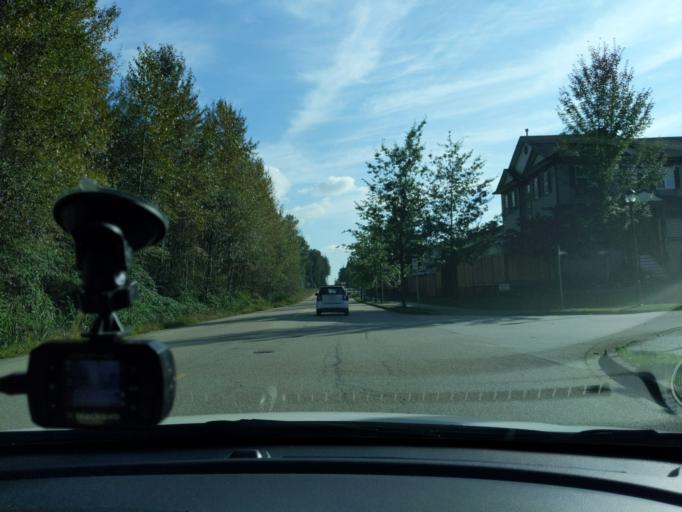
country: CA
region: British Columbia
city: Pitt Meadows
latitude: 49.2048
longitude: -122.6783
